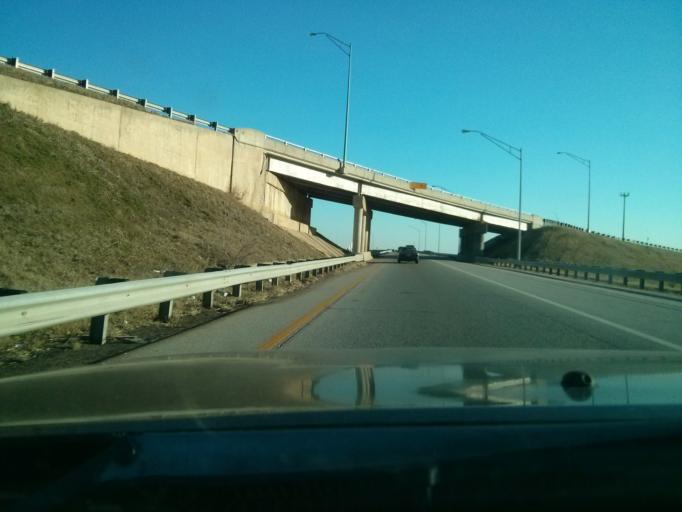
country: US
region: Oklahoma
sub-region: Tulsa County
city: Owasso
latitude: 36.1648
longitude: -95.8830
